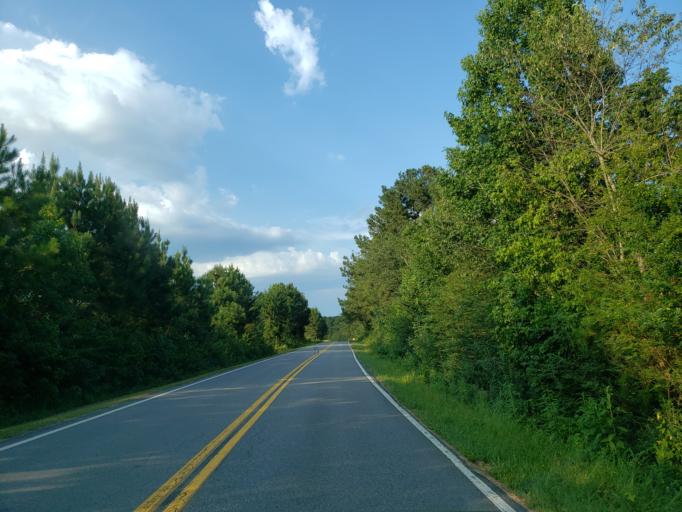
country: US
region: Georgia
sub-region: Polk County
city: Rockmart
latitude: 33.9789
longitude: -85.0032
